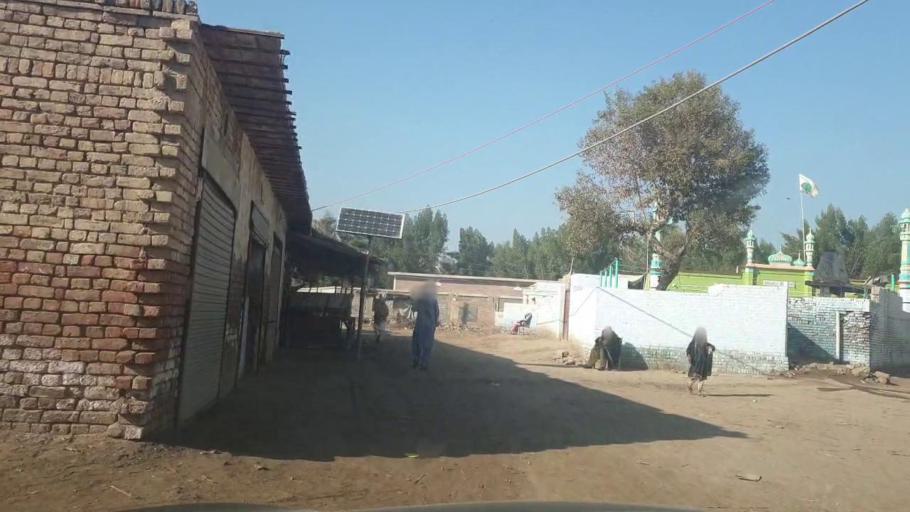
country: PK
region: Sindh
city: Mirpur Mathelo
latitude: 28.0792
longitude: 69.4672
